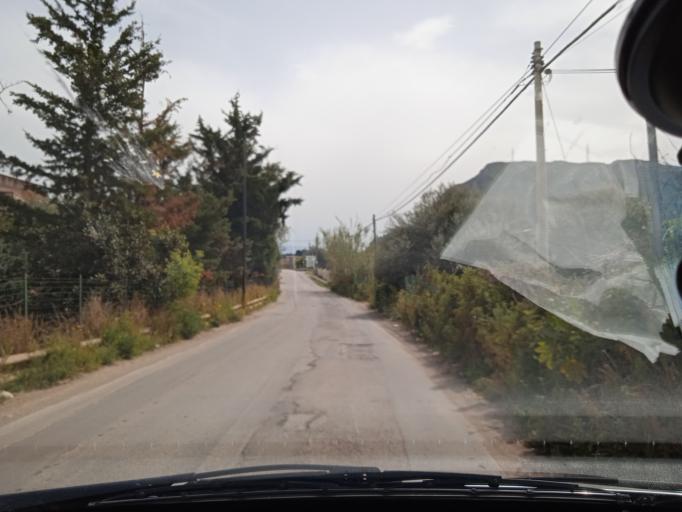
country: IT
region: Sicily
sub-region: Palermo
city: Torre Colonna-Sperone
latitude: 38.0287
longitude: 13.5717
